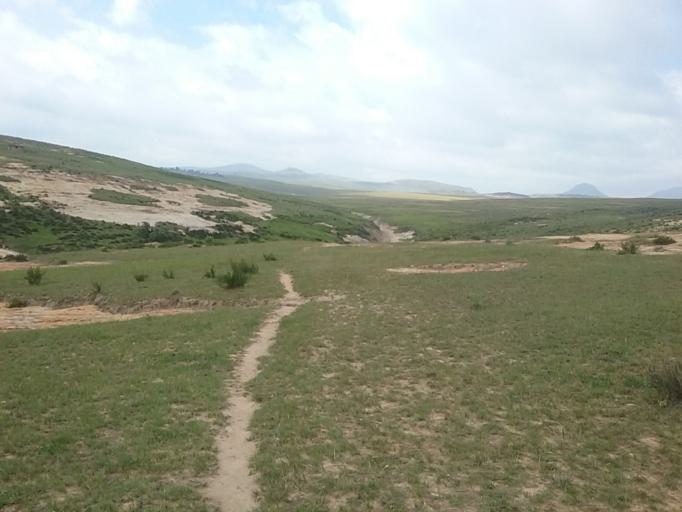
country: LS
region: Berea
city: Teyateyaneng
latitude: -29.1756
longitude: 27.8456
